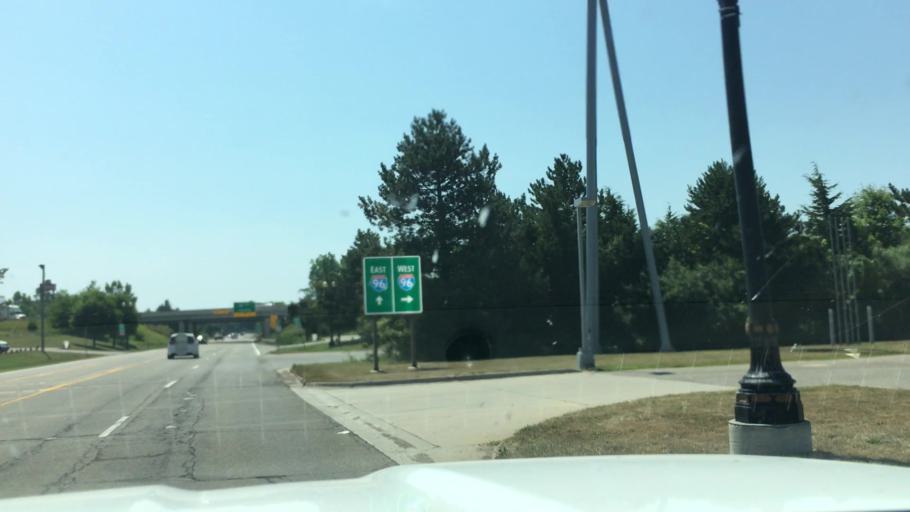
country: US
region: Michigan
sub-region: Ionia County
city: Portland
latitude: 42.8613
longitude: -84.8859
